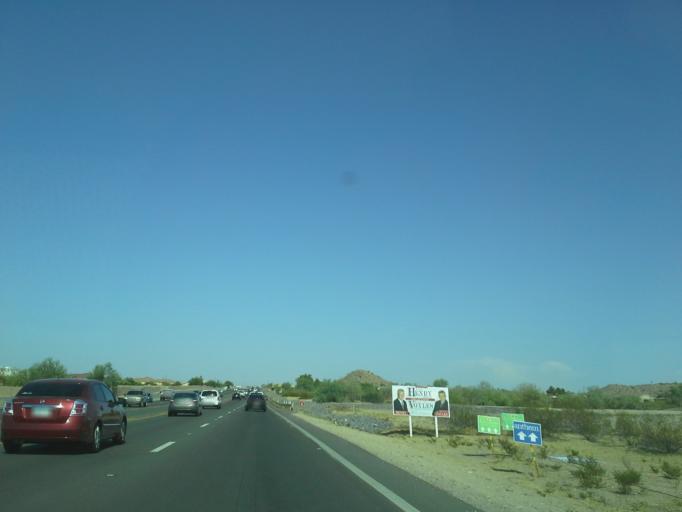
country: US
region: Arizona
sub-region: Maricopa County
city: Queen Creek
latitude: 33.2013
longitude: -111.6314
